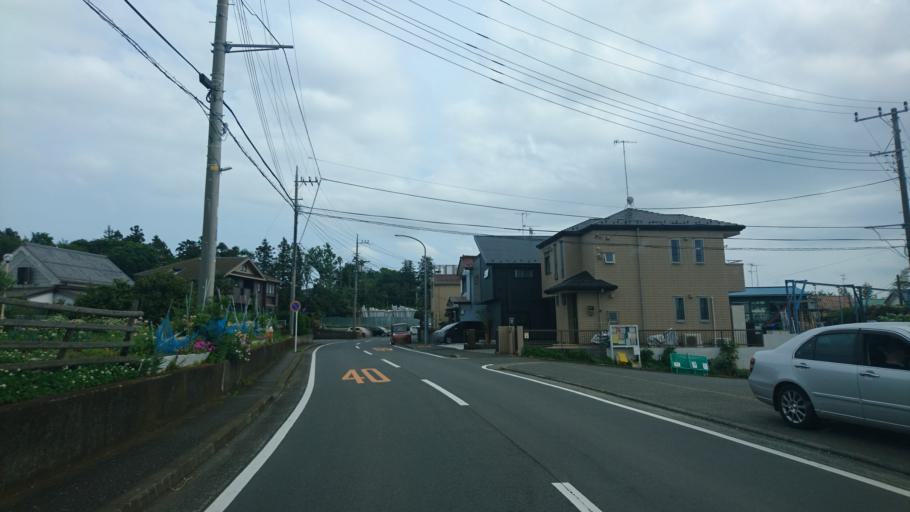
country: JP
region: Kanagawa
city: Fujisawa
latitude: 35.3978
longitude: 139.4795
